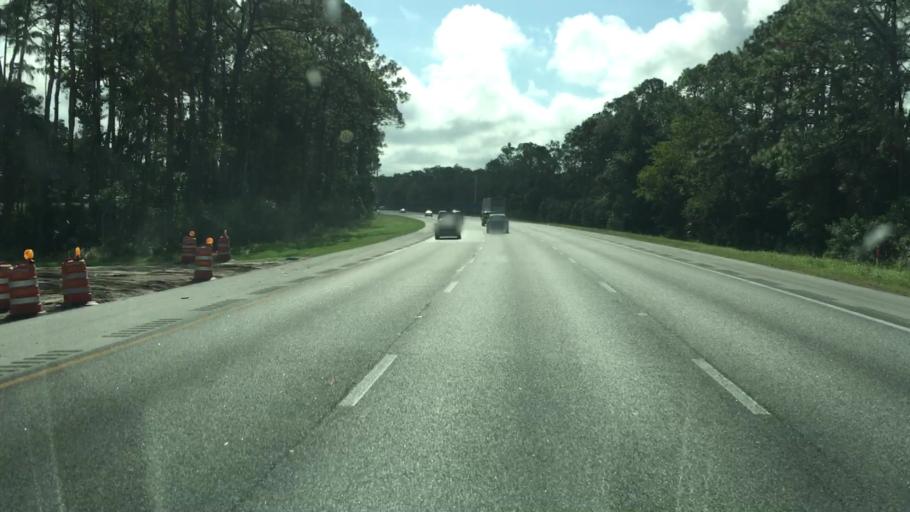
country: US
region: Florida
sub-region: Volusia County
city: South Daytona
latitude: 29.1326
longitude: -81.0627
